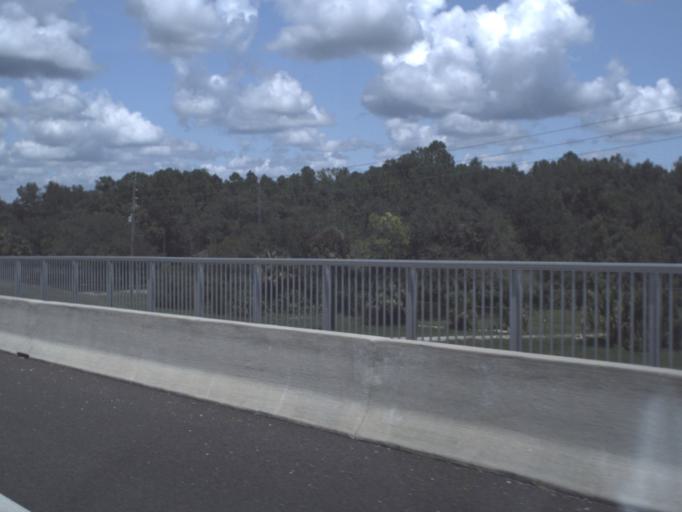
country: US
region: Florida
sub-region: Levy County
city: Inglis
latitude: 29.0146
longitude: -82.6647
